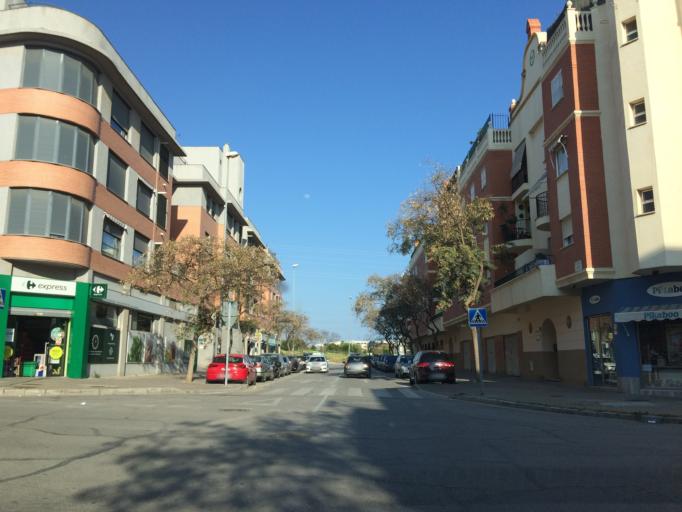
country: ES
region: Andalusia
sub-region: Provincia de Malaga
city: Malaga
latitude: 36.7233
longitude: -4.4757
